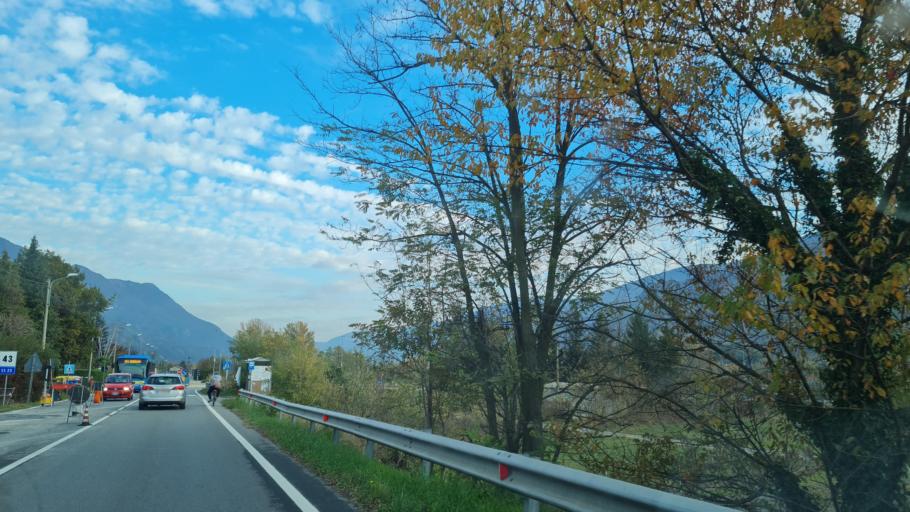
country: IT
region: Piedmont
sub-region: Provincia di Torino
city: San Giorio
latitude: 45.1361
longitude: 7.1729
